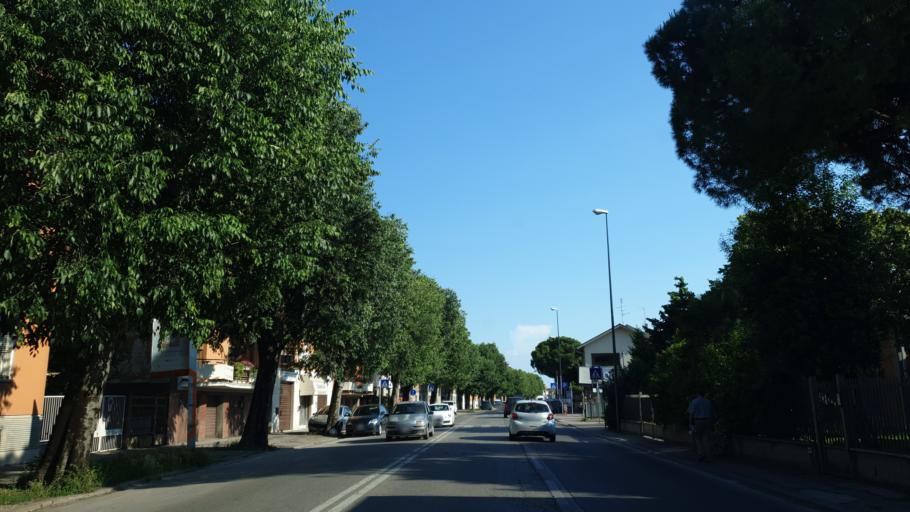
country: IT
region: Emilia-Romagna
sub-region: Provincia di Ravenna
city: Ravenna
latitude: 44.4154
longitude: 12.2106
